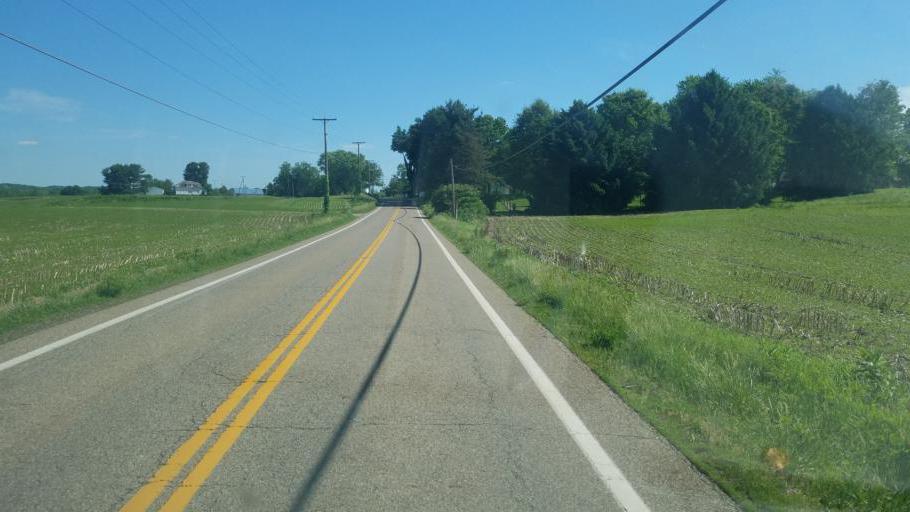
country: US
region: Ohio
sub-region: Coshocton County
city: West Lafayette
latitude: 40.2291
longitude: -81.7319
